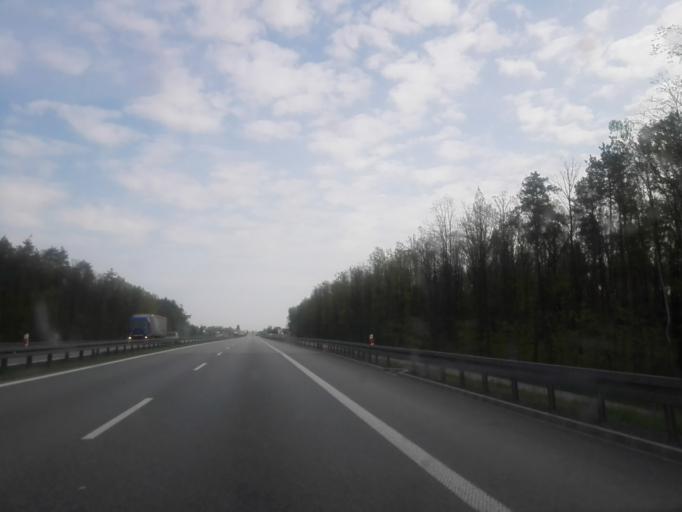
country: PL
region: Lodz Voivodeship
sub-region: Powiat rawski
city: Rawa Mazowiecka
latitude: 51.7293
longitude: 20.2282
